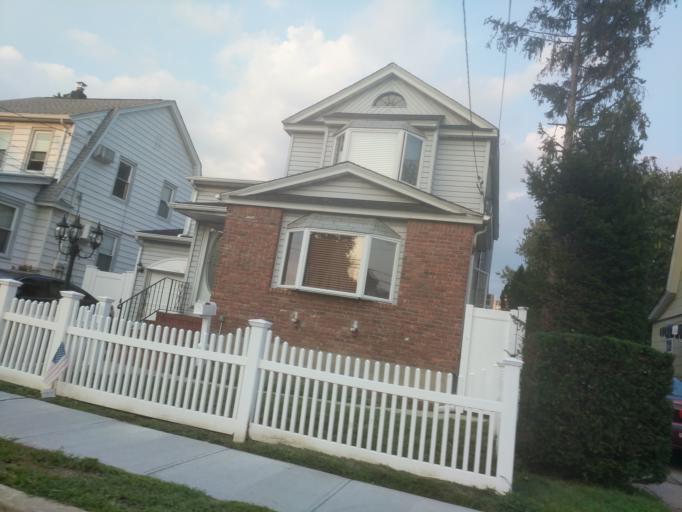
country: US
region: New York
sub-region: Nassau County
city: Valley Stream
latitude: 40.6592
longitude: -73.7057
